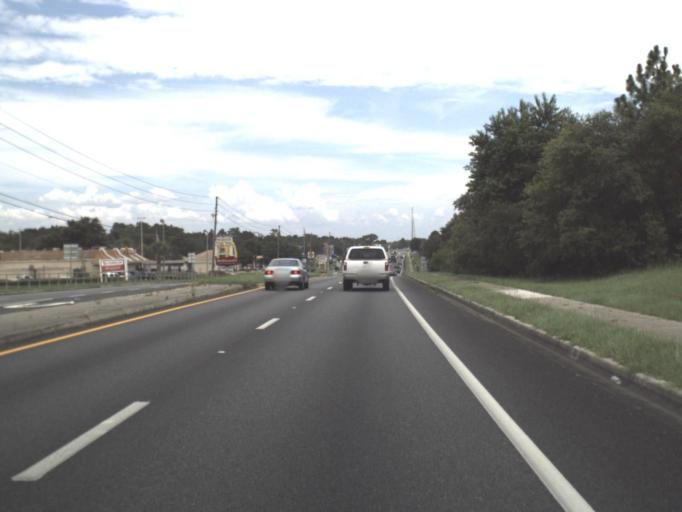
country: US
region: Florida
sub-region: Citrus County
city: Inverness Highlands North
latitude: 28.8540
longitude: -82.3894
